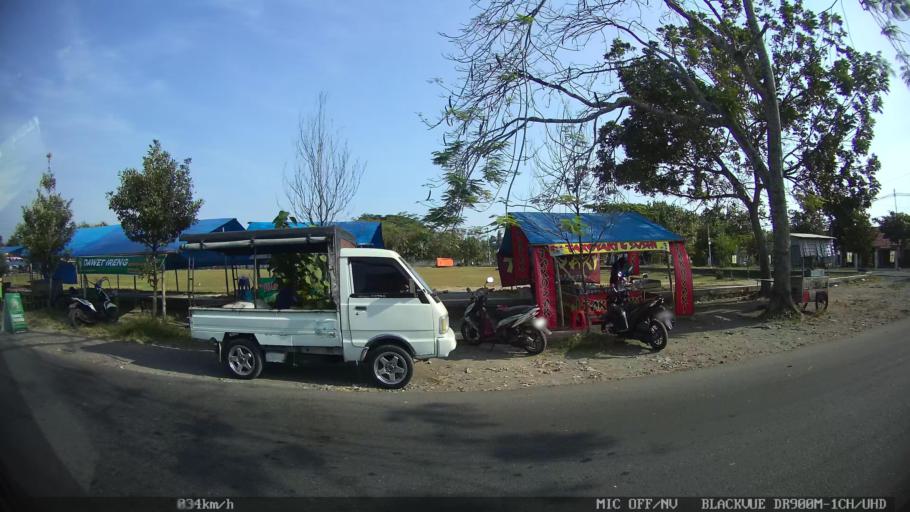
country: ID
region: Daerah Istimewa Yogyakarta
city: Pandak
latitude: -7.9000
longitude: 110.2977
